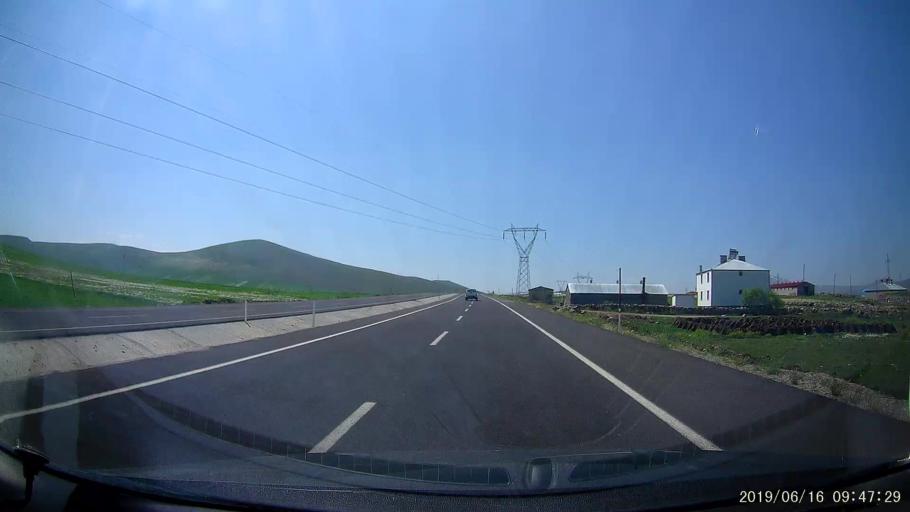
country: TR
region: Kars
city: Digor
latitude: 40.4470
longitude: 43.3441
